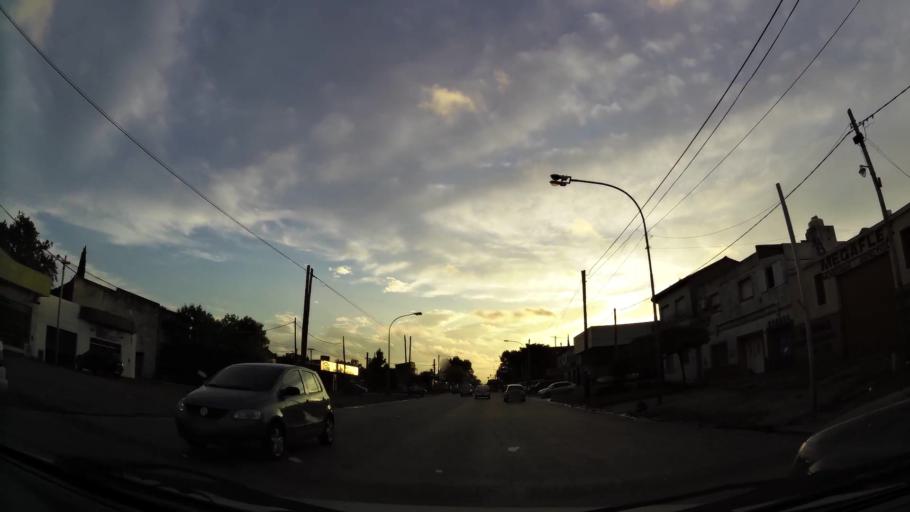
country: AR
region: Buenos Aires
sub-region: Partido de Lomas de Zamora
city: Lomas de Zamora
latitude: -34.7655
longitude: -58.3698
